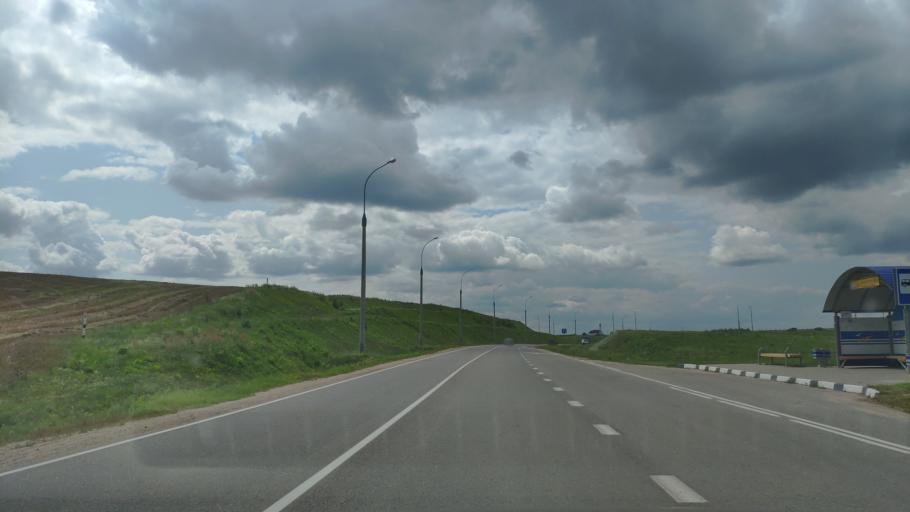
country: BY
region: Minsk
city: Zaslawye
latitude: 54.0066
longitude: 27.3149
